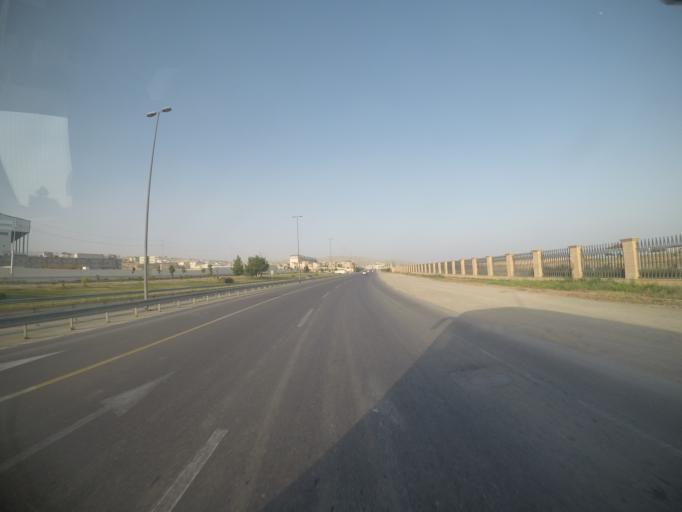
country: AZ
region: Baki
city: Badamdar
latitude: 40.3047
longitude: 49.7811
